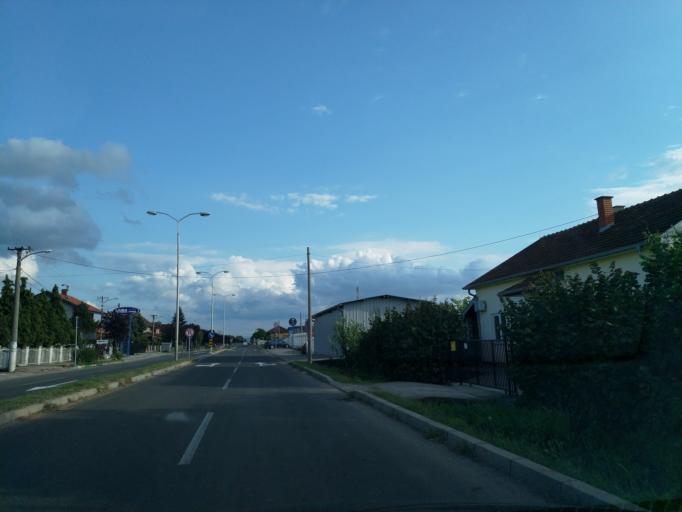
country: RS
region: Central Serbia
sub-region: Pomoravski Okrug
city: Paracin
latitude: 43.8446
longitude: 21.4144
